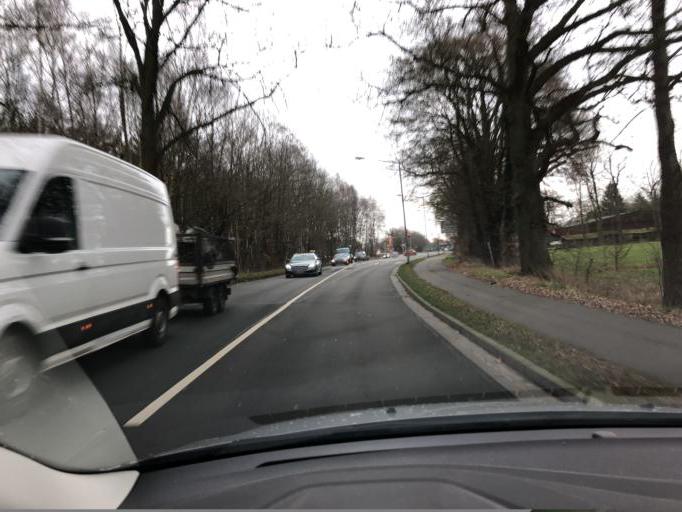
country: DE
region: Lower Saxony
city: Oldenburg
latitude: 53.1624
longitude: 8.1658
